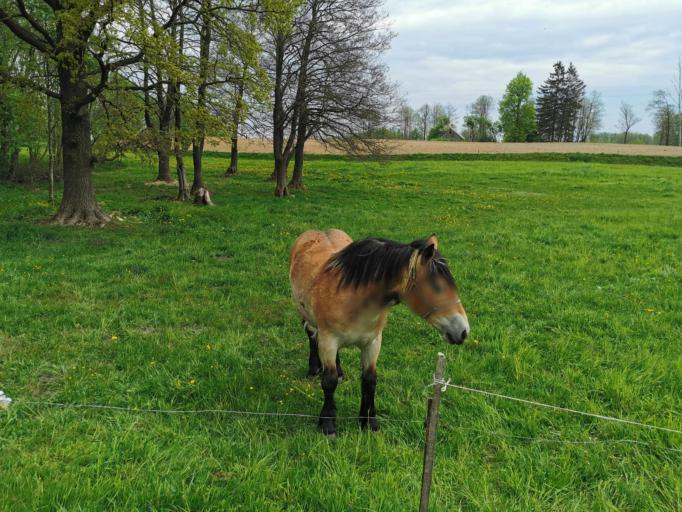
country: PL
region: Podlasie
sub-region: Powiat suwalski
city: Filipow
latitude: 54.0956
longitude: 22.7121
